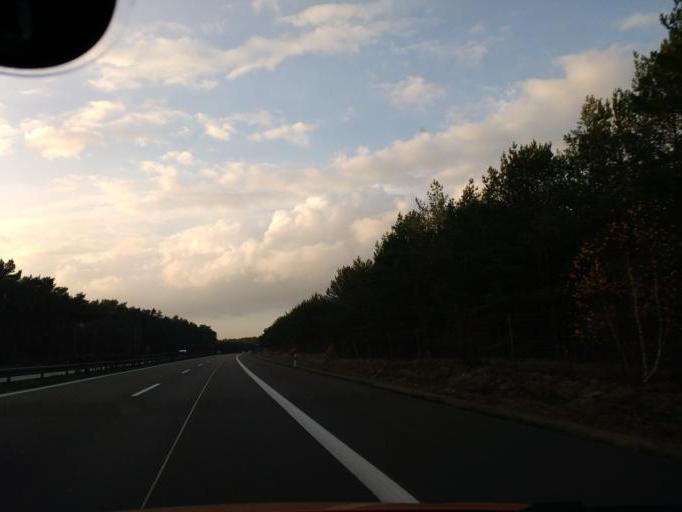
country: DE
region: Mecklenburg-Vorpommern
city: Neustadt-Glewe
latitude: 53.3720
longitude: 11.6447
